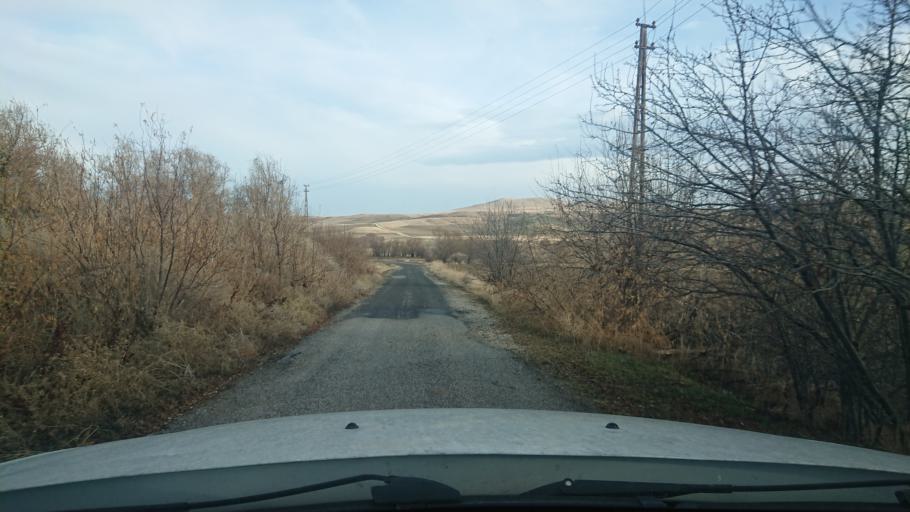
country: TR
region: Aksaray
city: Acipinar
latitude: 38.6764
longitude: 33.8667
